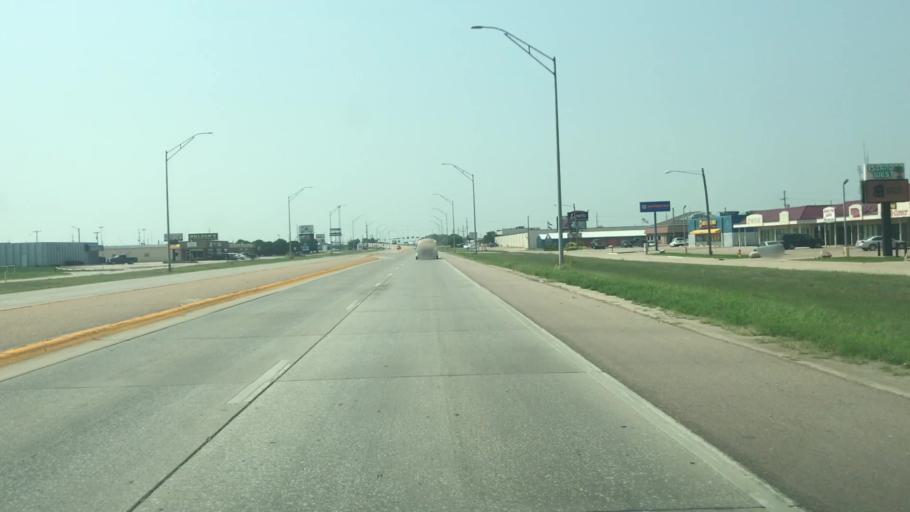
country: US
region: Nebraska
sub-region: Hall County
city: Grand Island
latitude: 40.9159
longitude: -98.3718
